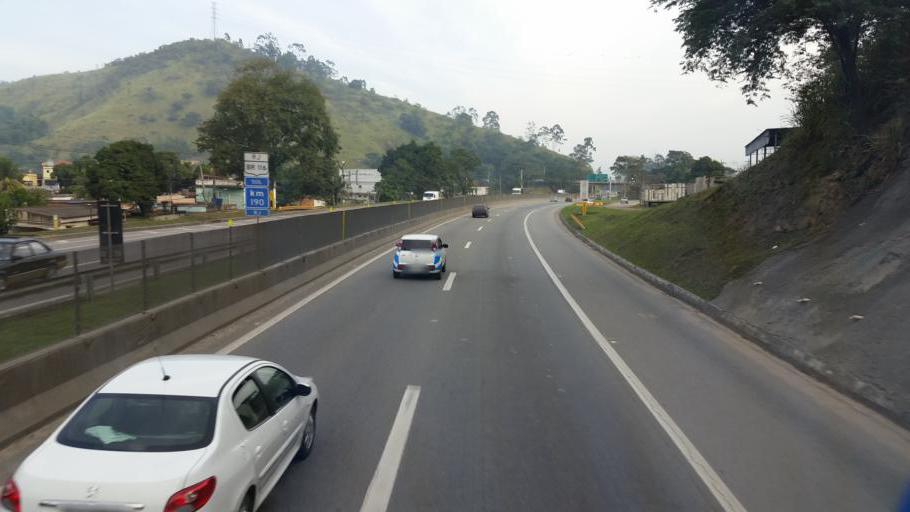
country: BR
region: Rio de Janeiro
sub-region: Queimados
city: Queimados
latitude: -22.7349
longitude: -43.5543
